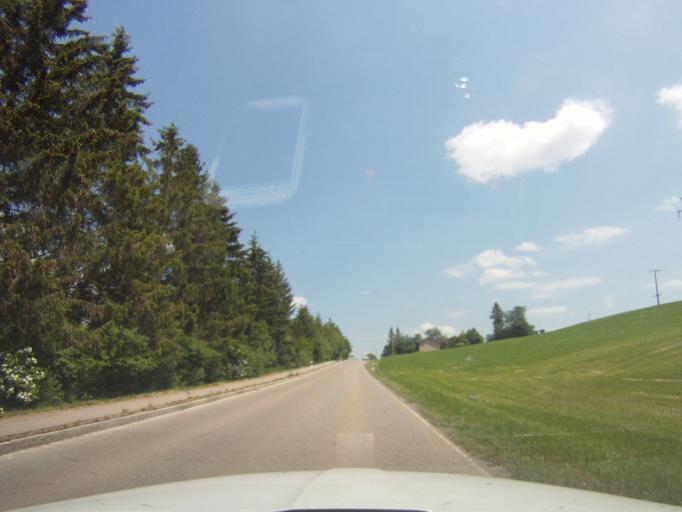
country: DE
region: Bavaria
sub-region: Swabia
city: Oy-Mittelberg
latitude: 47.6089
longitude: 10.4463
